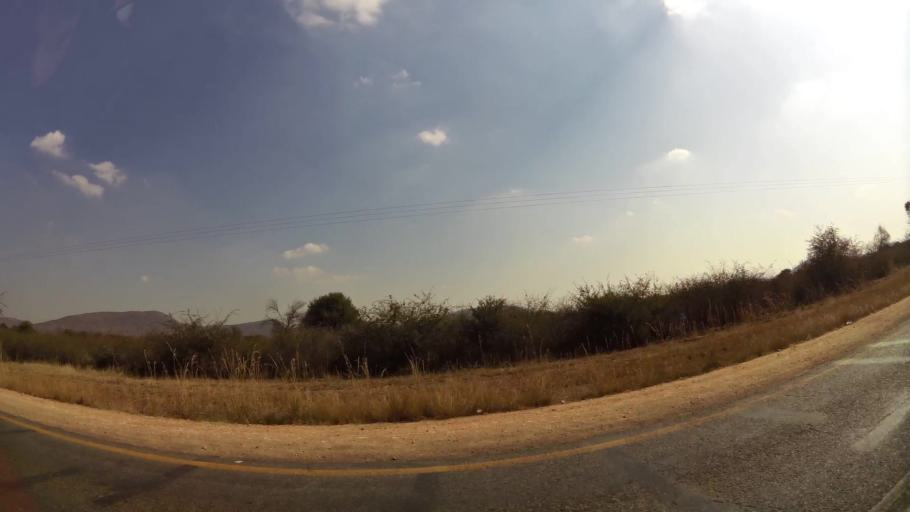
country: ZA
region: North-West
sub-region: Bojanala Platinum District Municipality
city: Mogwase
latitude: -25.4700
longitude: 27.0872
